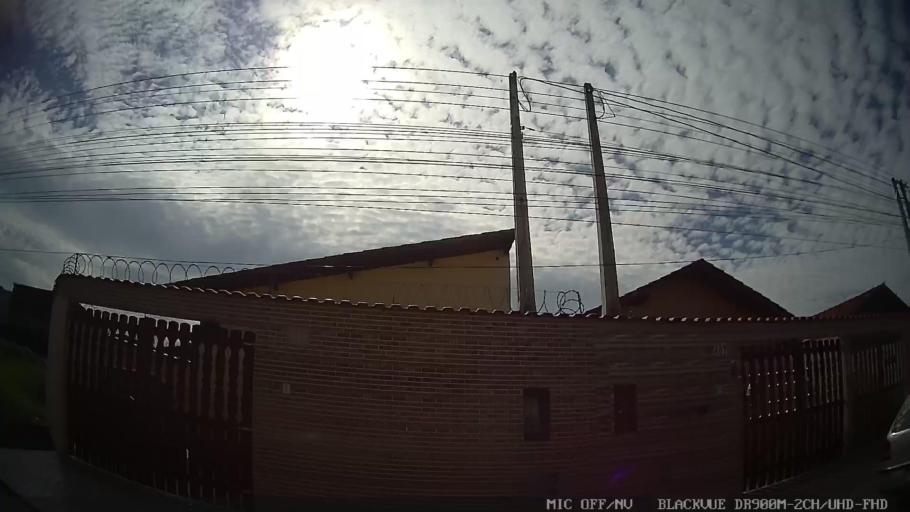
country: BR
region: Sao Paulo
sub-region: Itanhaem
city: Itanhaem
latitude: -24.1614
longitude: -46.7576
